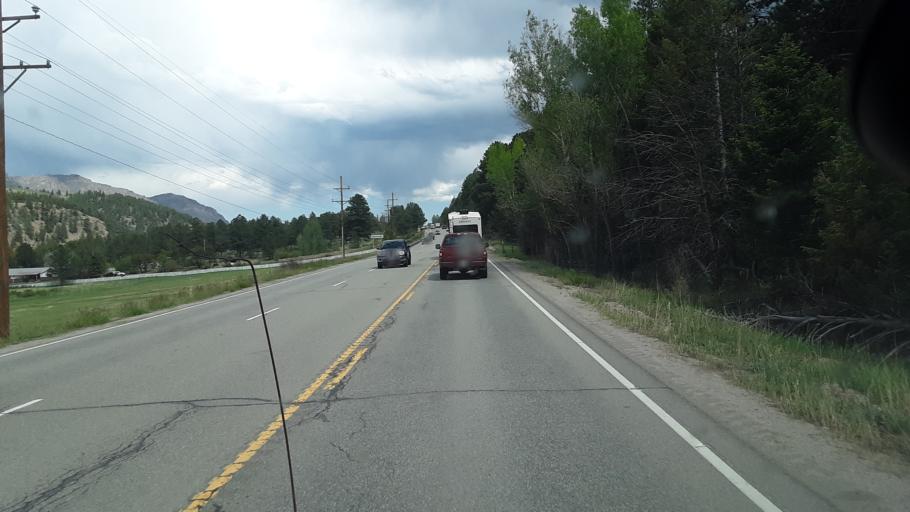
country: US
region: Colorado
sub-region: Clear Creek County
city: Georgetown
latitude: 39.4343
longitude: -105.5859
